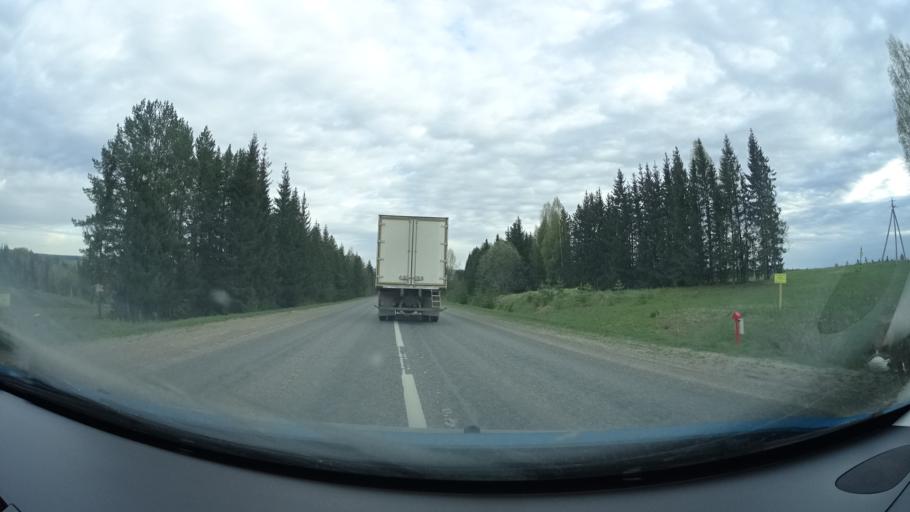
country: RU
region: Perm
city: Yugo-Kamskiy
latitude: 57.5761
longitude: 55.6817
